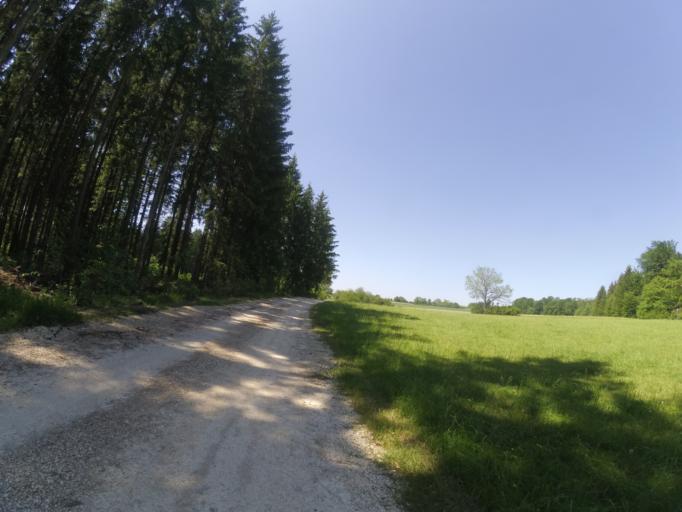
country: DE
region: Baden-Wuerttemberg
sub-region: Tuebingen Region
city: Merklingen
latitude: 48.4957
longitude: 9.7857
